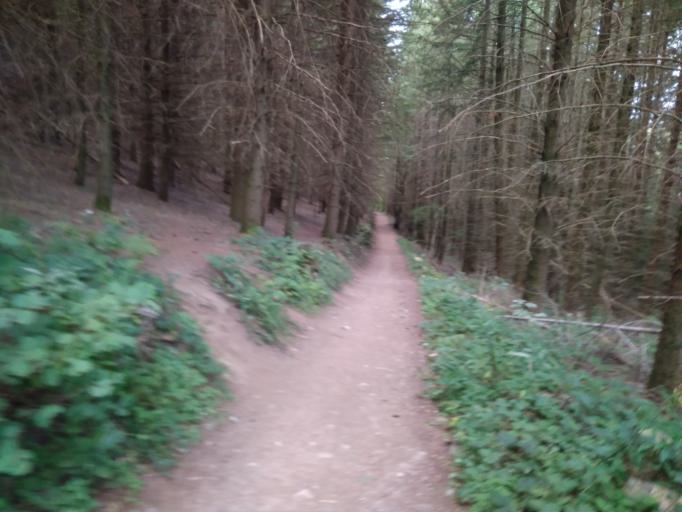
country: FR
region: Auvergne
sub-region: Departement de l'Allier
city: Le Mayet-de-Montagne
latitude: 46.1263
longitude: 3.7628
